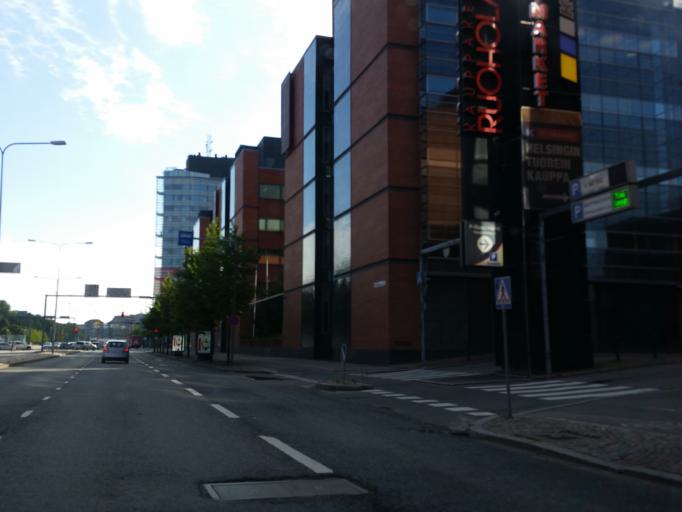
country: FI
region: Uusimaa
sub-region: Helsinki
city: Helsinki
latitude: 60.1642
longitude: 24.9096
